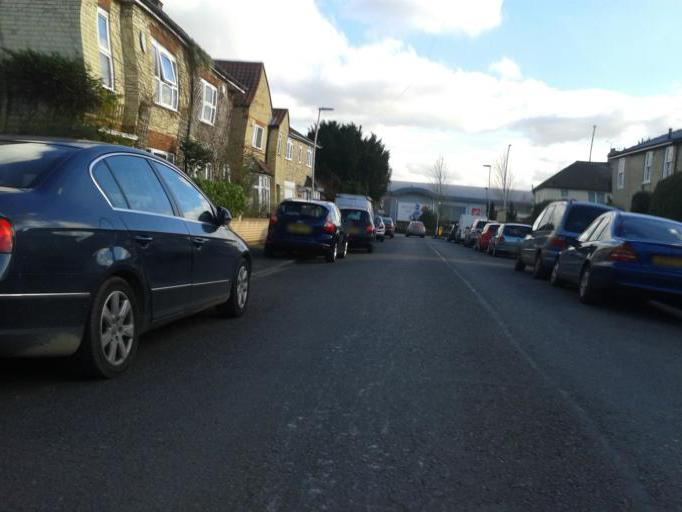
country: GB
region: England
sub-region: Cambridgeshire
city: Cambridge
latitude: 52.2135
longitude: 0.1488
